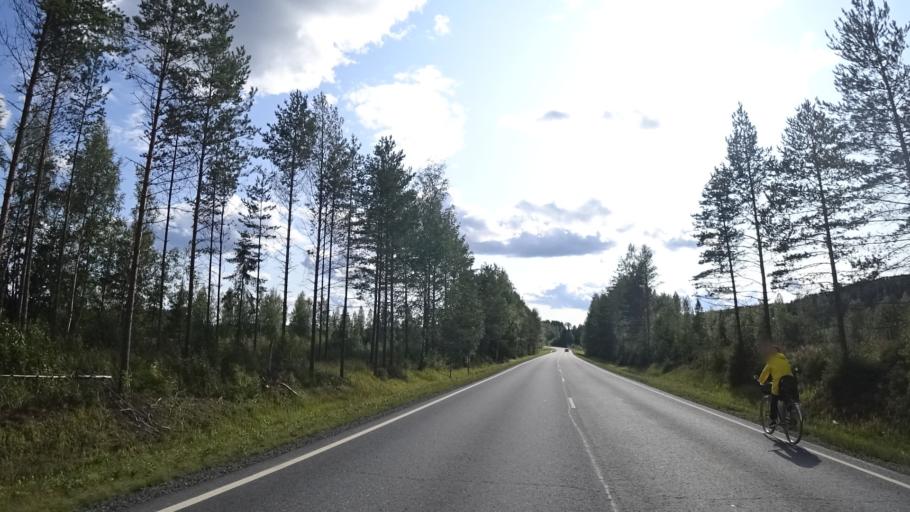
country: FI
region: North Karelia
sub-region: Keski-Karjala
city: Tohmajaervi
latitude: 62.2205
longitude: 30.3060
